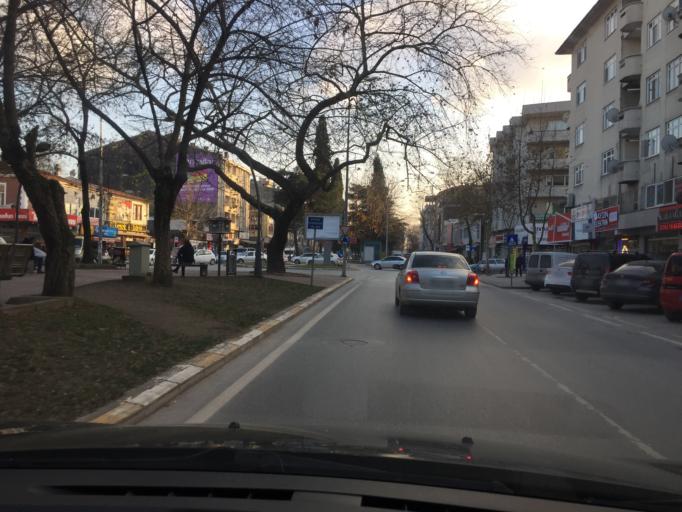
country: TR
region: Sakarya
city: Adapazari
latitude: 40.7835
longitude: 30.3996
